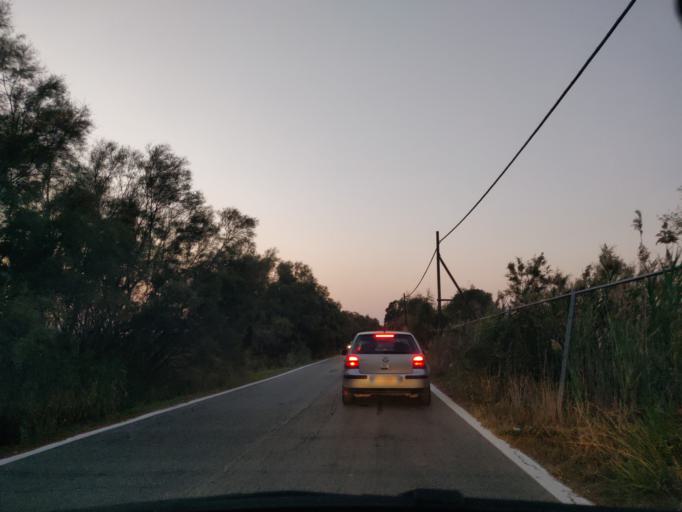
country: IT
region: Latium
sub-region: Citta metropolitana di Roma Capitale
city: Npp 23 (Parco Leonardo)
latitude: 41.8246
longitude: 12.2902
